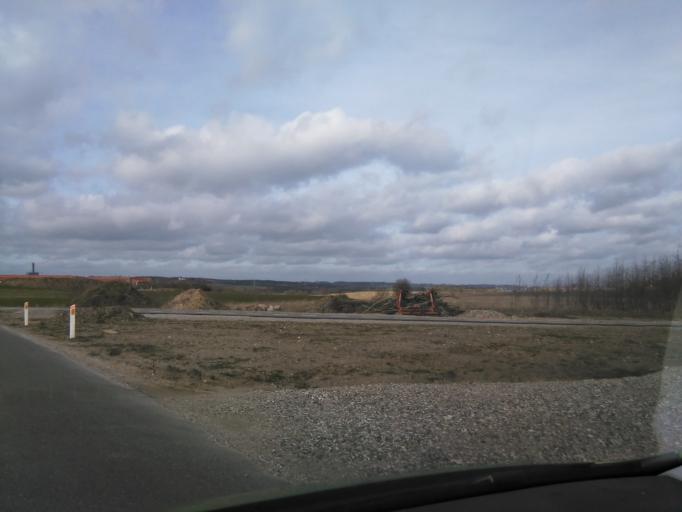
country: DK
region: Central Jutland
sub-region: Arhus Kommune
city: Trige
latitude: 56.1959
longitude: 10.1594
